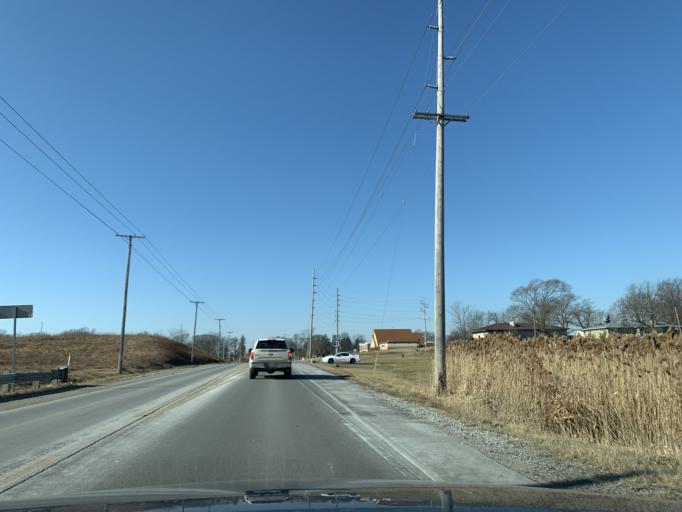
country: US
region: Indiana
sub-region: Lake County
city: Saint John
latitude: 41.4212
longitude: -87.4663
